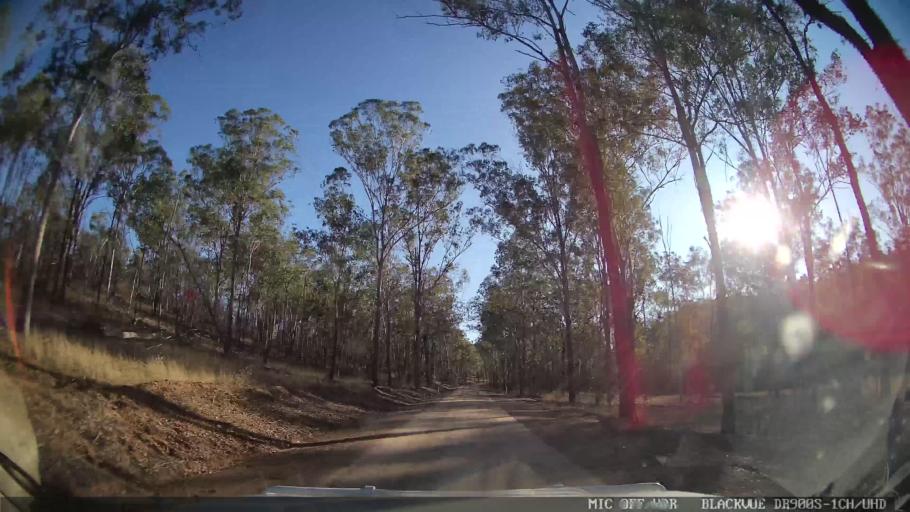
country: AU
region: Queensland
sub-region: Gladstone
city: Toolooa
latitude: -24.6949
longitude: 151.4112
